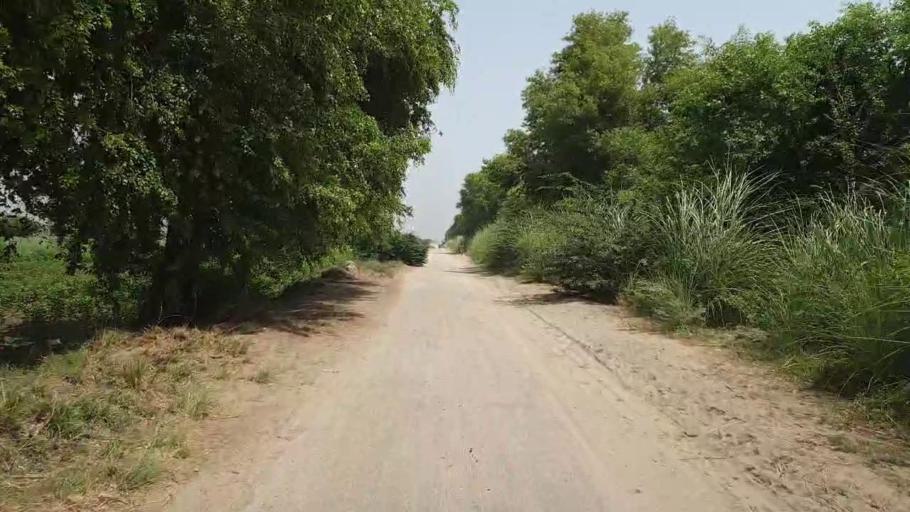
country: PK
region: Sindh
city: Nawabshah
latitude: 26.2939
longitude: 68.3074
